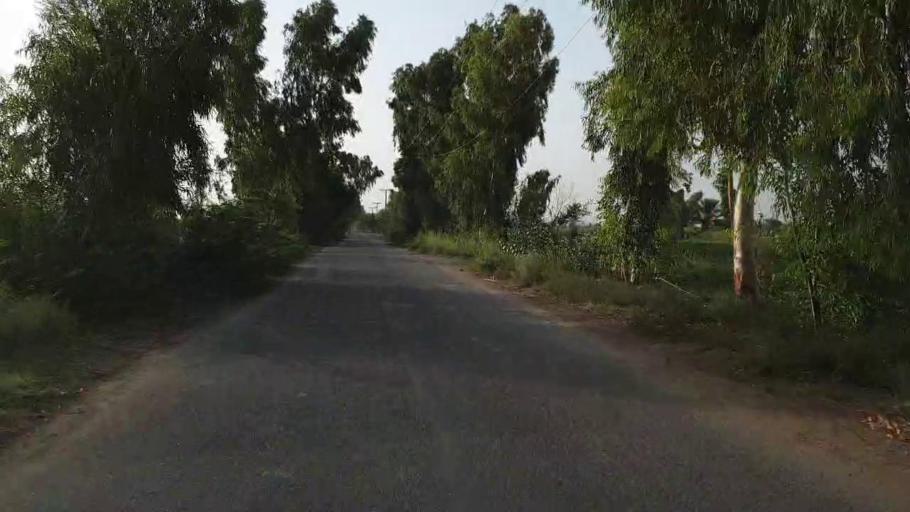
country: PK
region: Sindh
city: Bozdar
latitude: 27.1088
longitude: 68.9603
